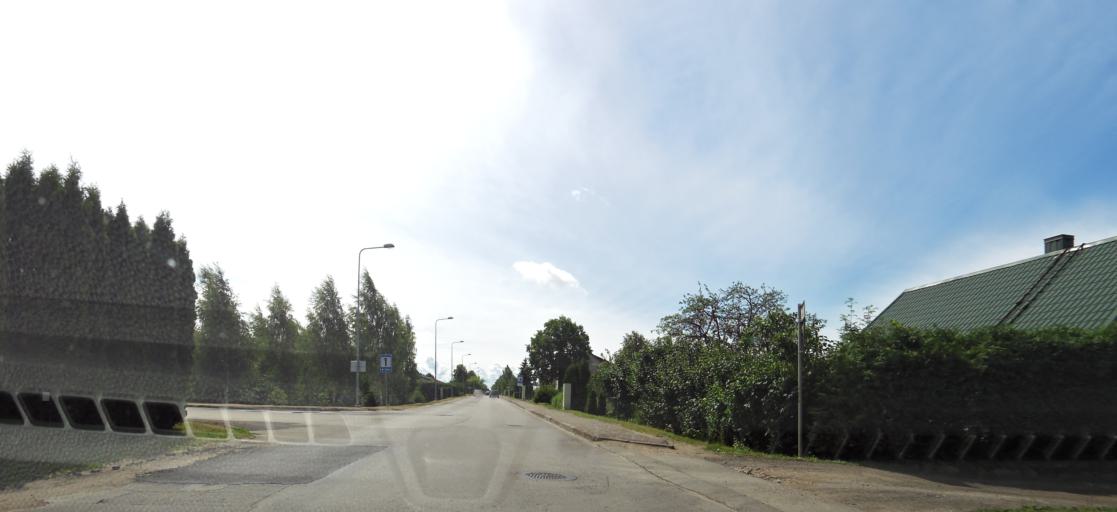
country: LT
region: Panevezys
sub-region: Birzai
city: Birzai
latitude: 56.1965
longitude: 24.7697
